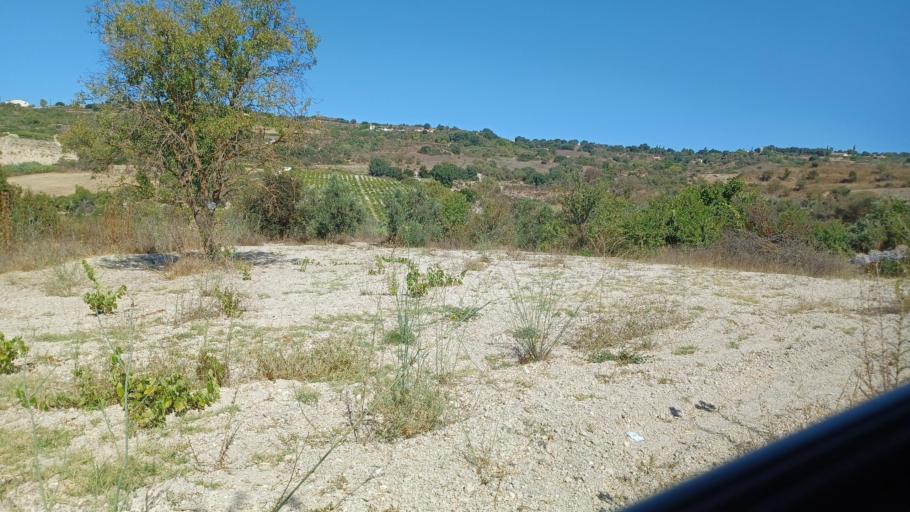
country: CY
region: Pafos
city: Mesogi
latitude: 34.8740
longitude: 32.5151
